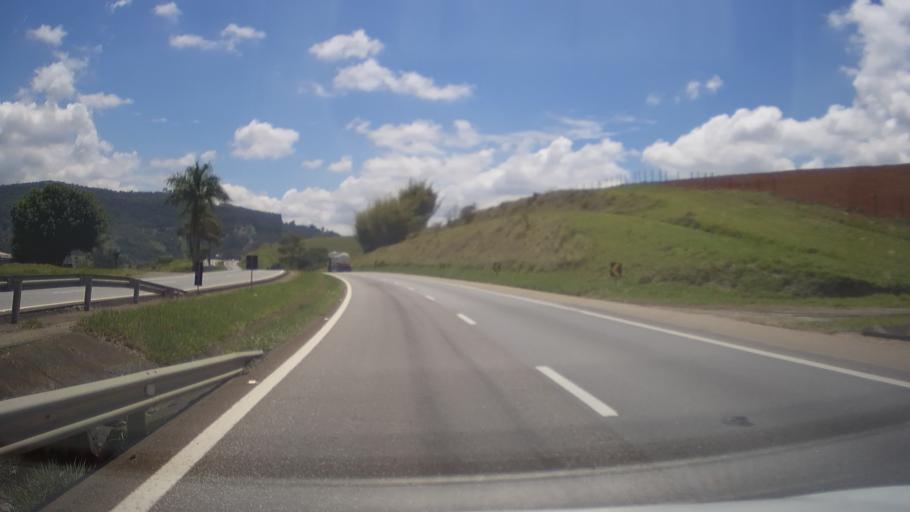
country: BR
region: Minas Gerais
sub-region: Campanha
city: Campanha
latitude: -21.8223
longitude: -45.4942
